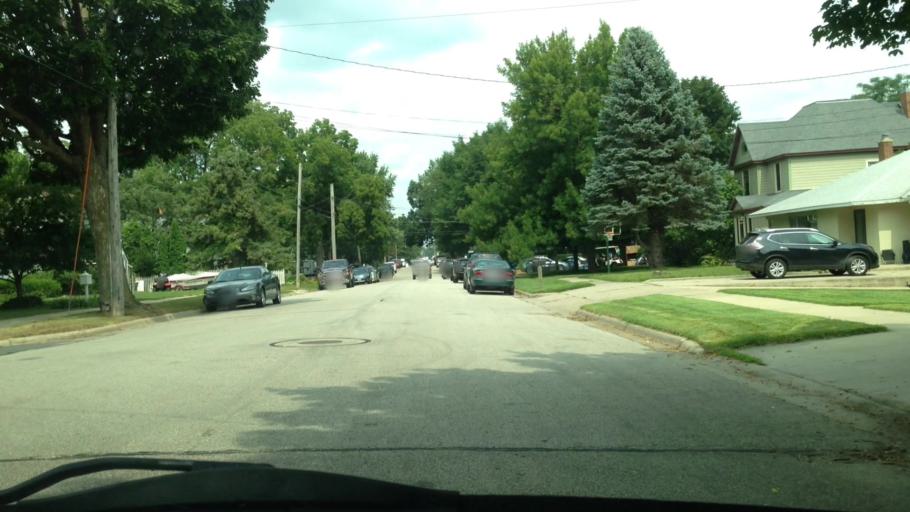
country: US
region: Minnesota
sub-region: Wabasha County
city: Plainview
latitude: 44.1594
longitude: -92.1713
